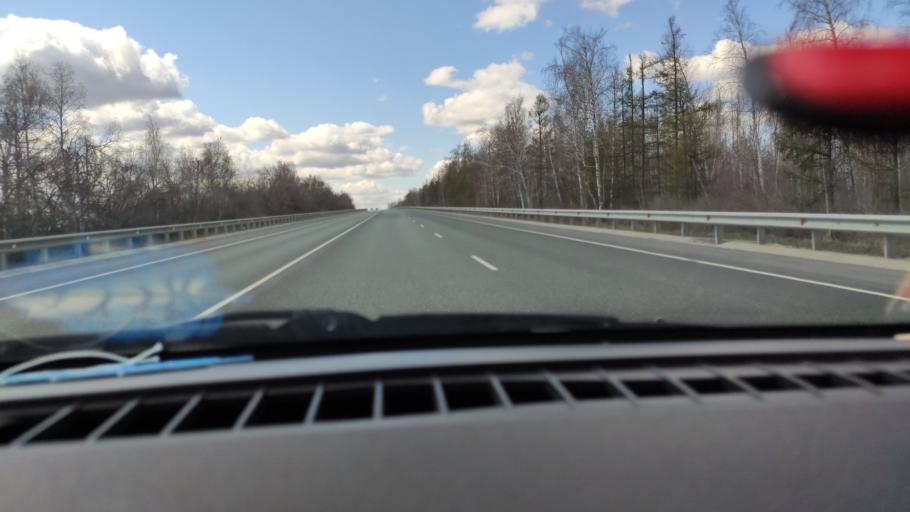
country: RU
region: Saratov
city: Khvalynsk
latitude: 52.5594
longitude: 48.0864
